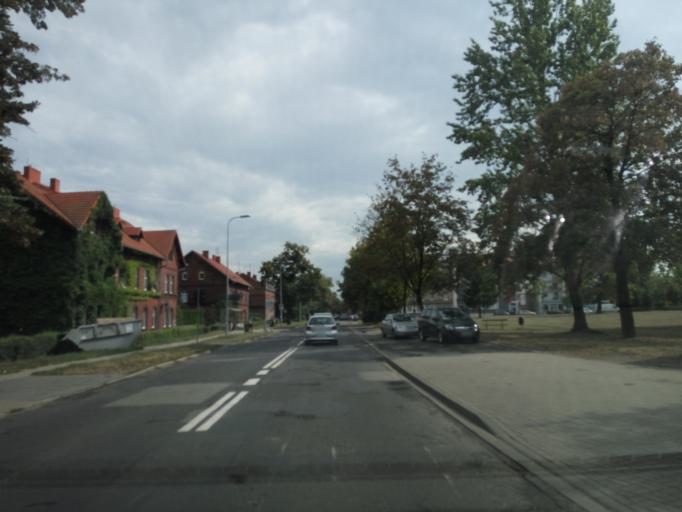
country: PL
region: Lower Silesian Voivodeship
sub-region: Powiat wroclawski
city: Radwanice
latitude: 51.0642
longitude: 17.0832
